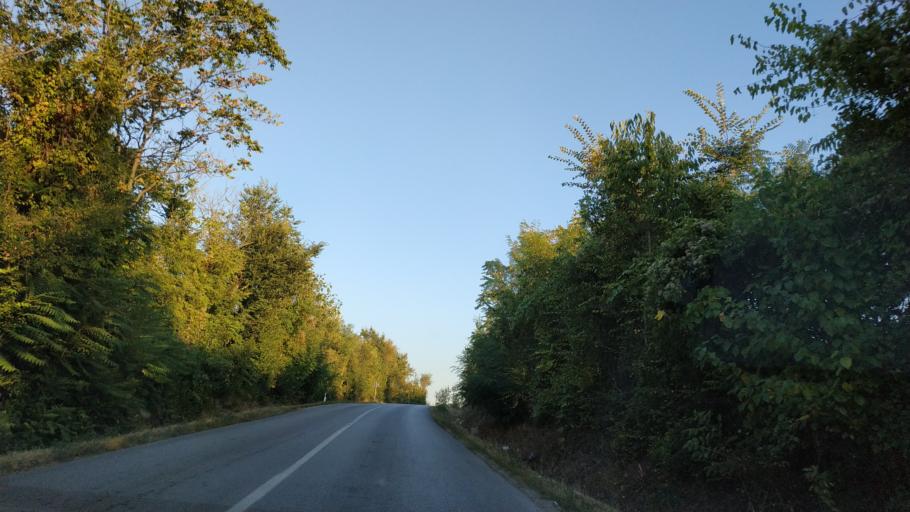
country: RS
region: Central Serbia
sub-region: Sumadijski Okrug
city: Raca
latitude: 44.2389
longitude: 20.8409
